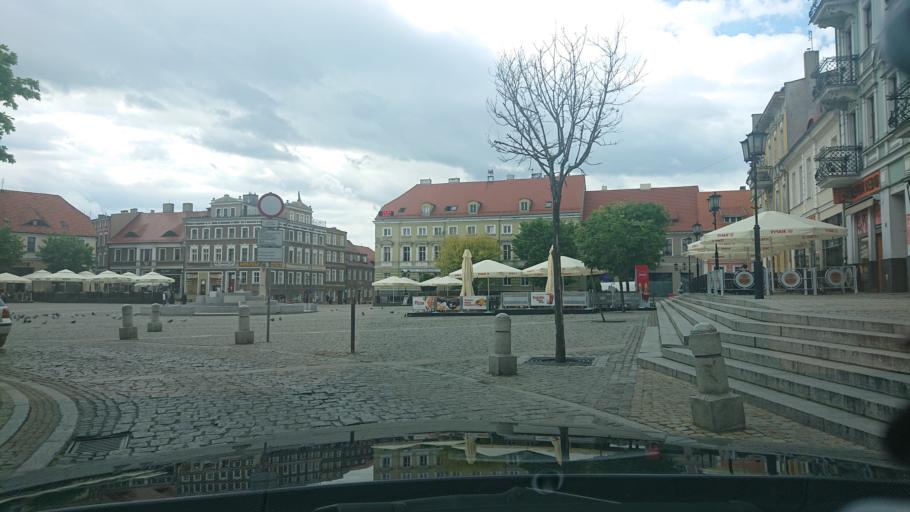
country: PL
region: Greater Poland Voivodeship
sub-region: Powiat gnieznienski
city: Gniezno
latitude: 52.5362
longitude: 17.5967
